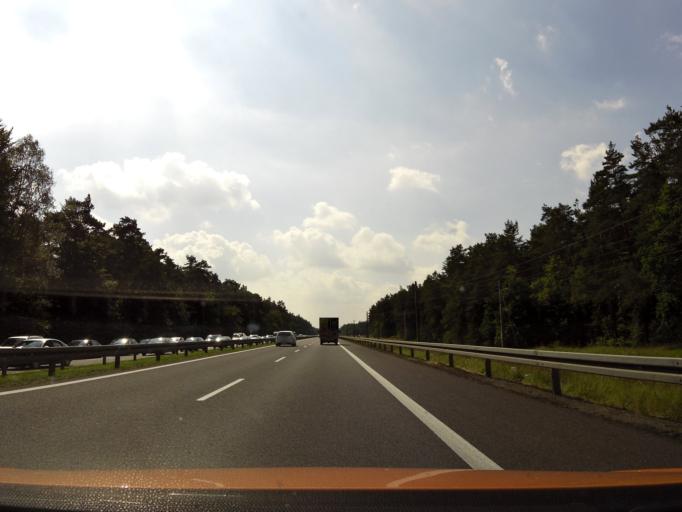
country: PL
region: West Pomeranian Voivodeship
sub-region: Powiat goleniowski
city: Goleniow
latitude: 53.5045
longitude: 14.8002
